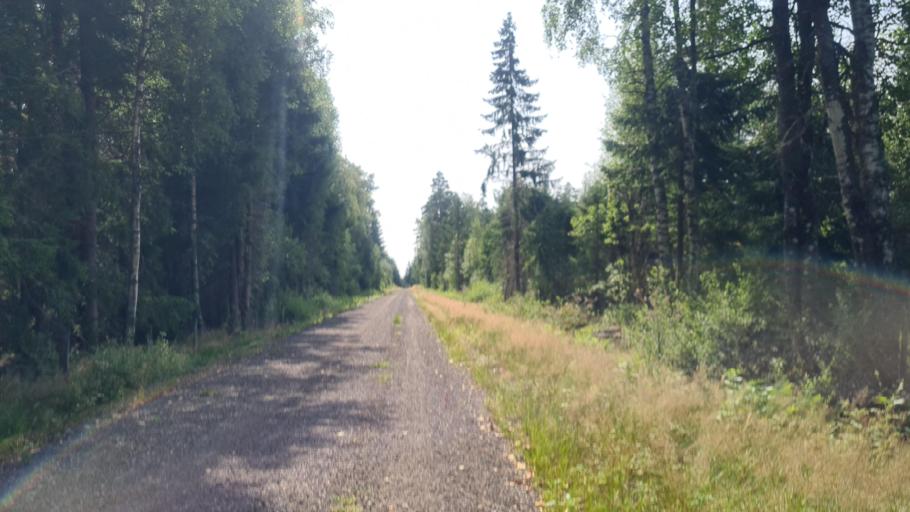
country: SE
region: Kronoberg
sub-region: Ljungby Kommun
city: Lagan
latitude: 56.9644
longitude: 13.9535
